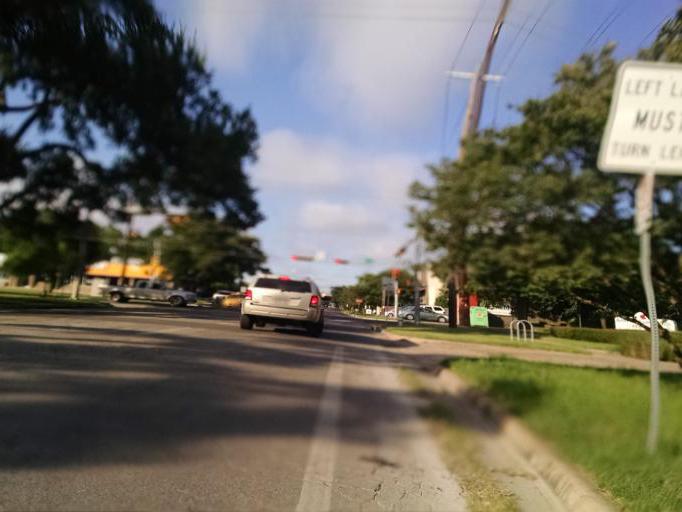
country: US
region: Texas
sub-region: Travis County
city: Austin
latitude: 30.3009
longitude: -97.7334
